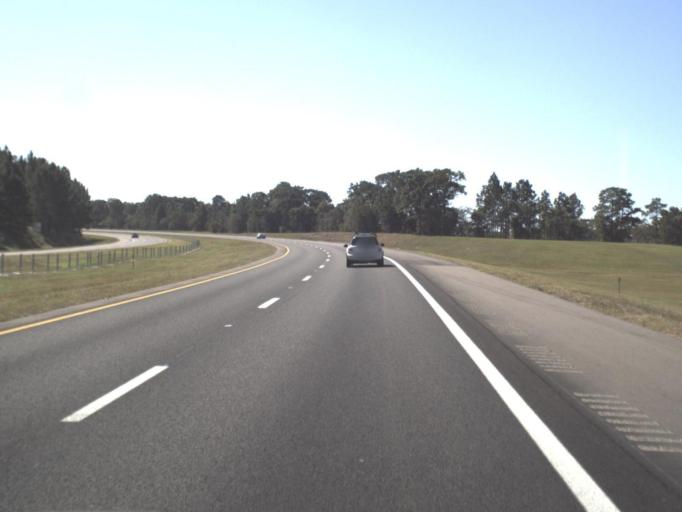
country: US
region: Florida
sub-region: Hernando County
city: Spring Hill
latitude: 28.4917
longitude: -82.4821
